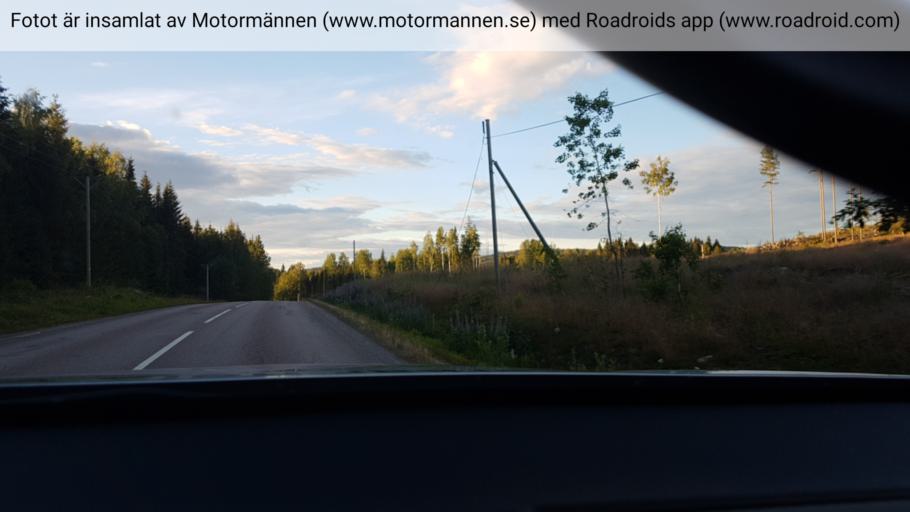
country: SE
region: Vaermland
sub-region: Torsby Kommun
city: Torsby
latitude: 60.0654
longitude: 13.0946
